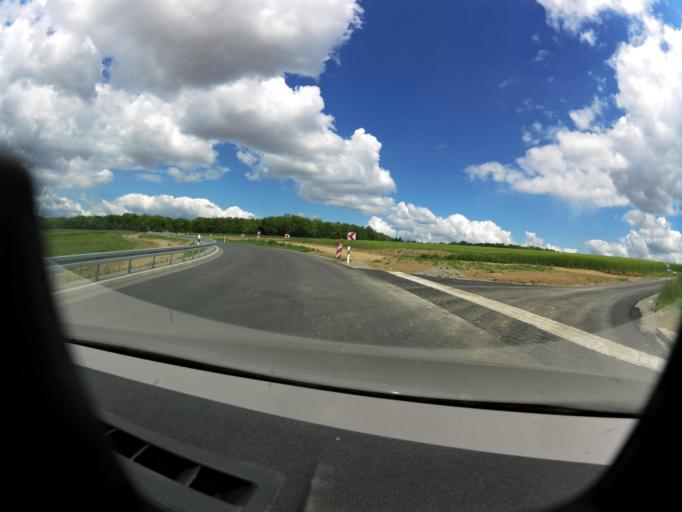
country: DE
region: Bavaria
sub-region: Regierungsbezirk Unterfranken
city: Schwanfeld
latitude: 49.9308
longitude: 10.1386
